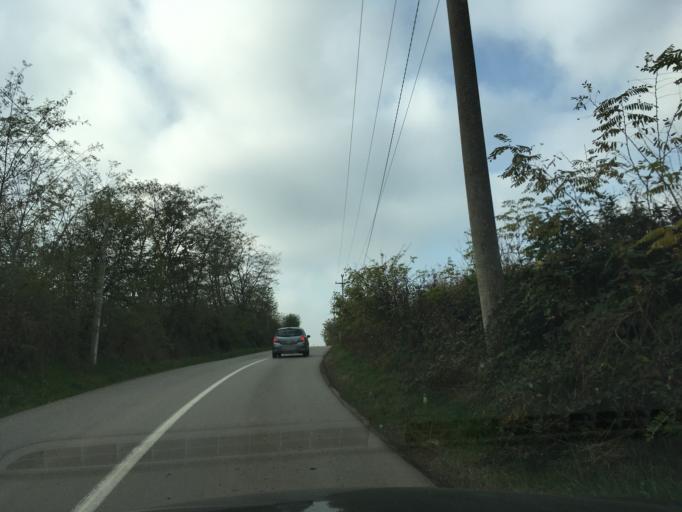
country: RS
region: Central Serbia
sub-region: Belgrade
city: Sopot
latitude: 44.4964
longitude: 20.6208
